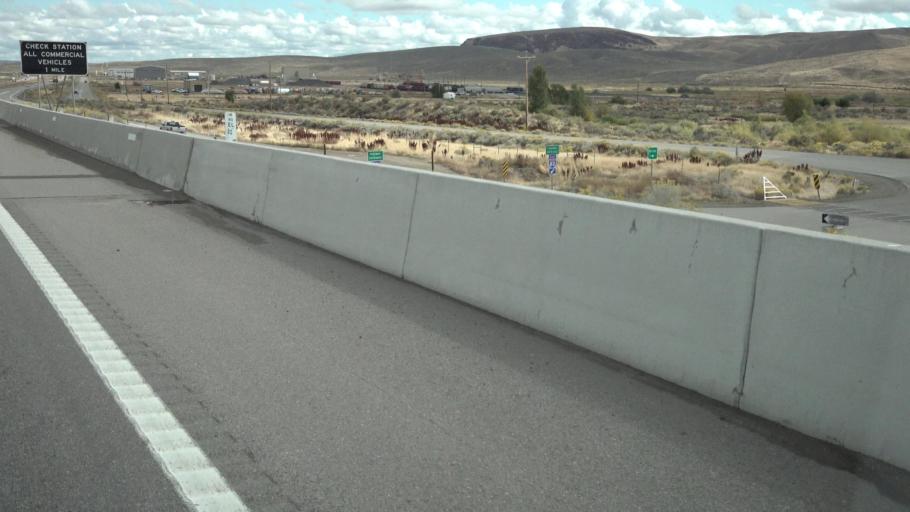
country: US
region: Nevada
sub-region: Elko County
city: Elko
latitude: 40.9335
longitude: -115.6658
